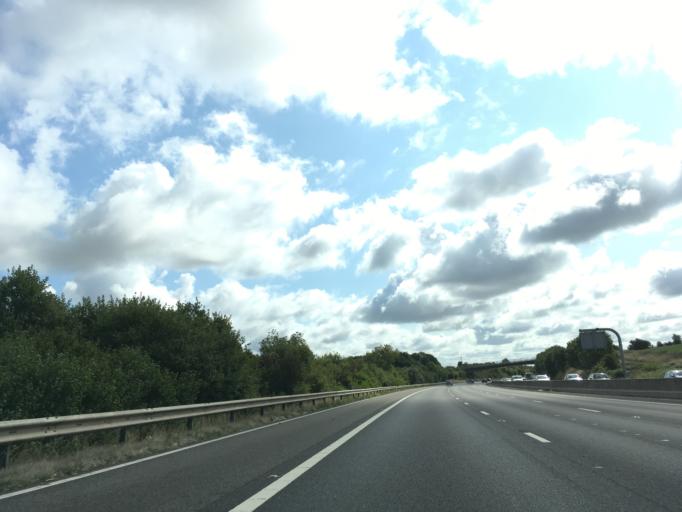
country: GB
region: England
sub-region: Wiltshire
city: Aldbourne
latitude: 51.5070
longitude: -1.6018
